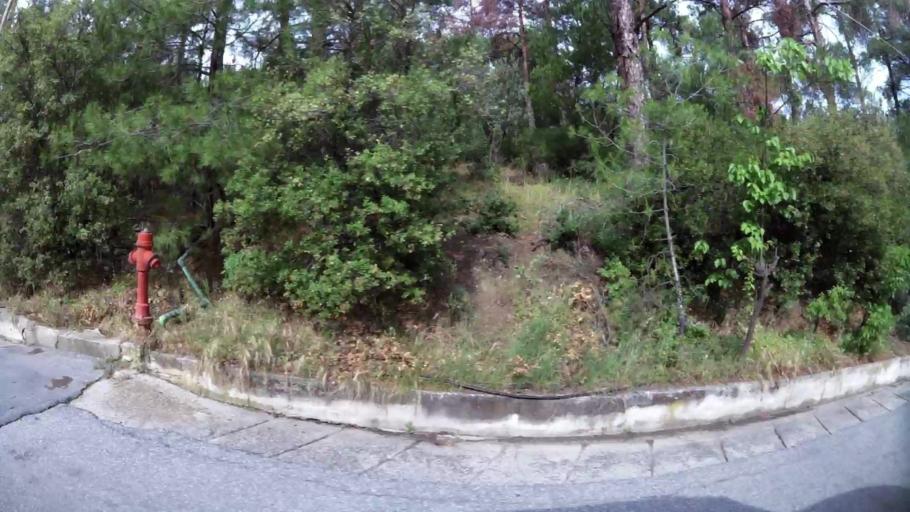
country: GR
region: Central Macedonia
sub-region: Nomos Thessalonikis
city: Panorama
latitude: 40.5892
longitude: 23.0327
